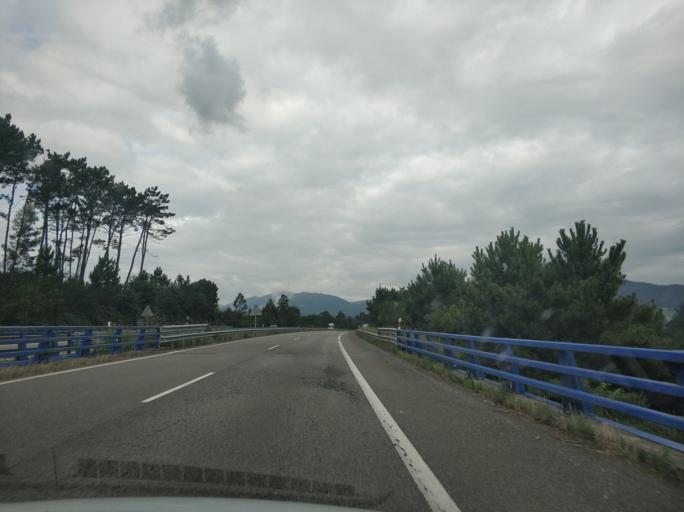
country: ES
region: Asturias
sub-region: Province of Asturias
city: Navia
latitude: 43.5298
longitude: -6.7109
